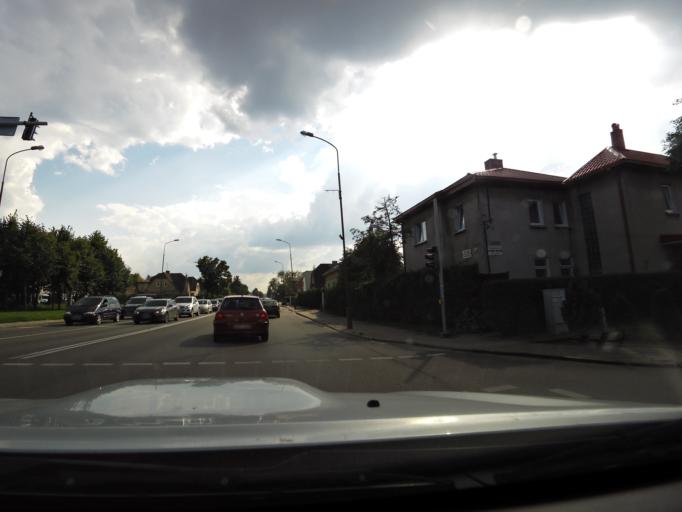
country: LT
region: Siauliu apskritis
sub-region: Siauliai
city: Siauliai
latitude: 55.9320
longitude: 23.3009
